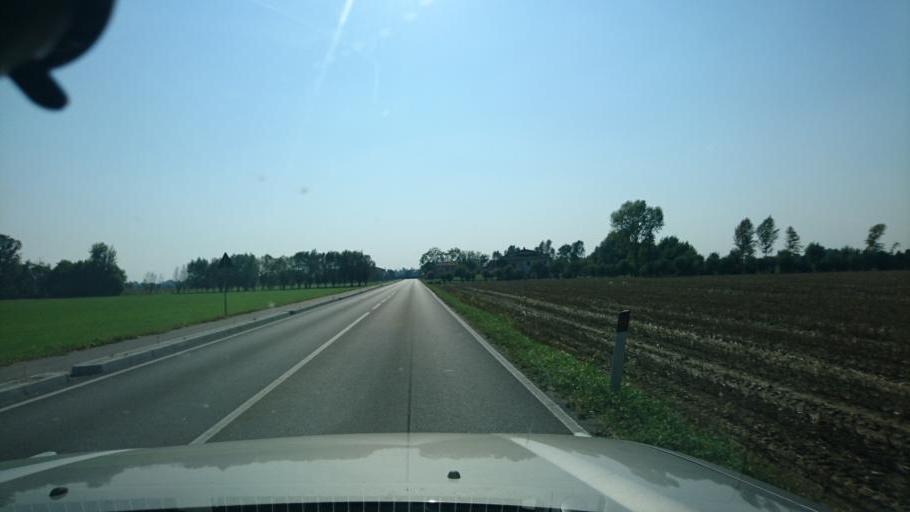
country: IT
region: Veneto
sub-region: Provincia di Padova
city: Gazzo
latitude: 45.5729
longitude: 11.7099
